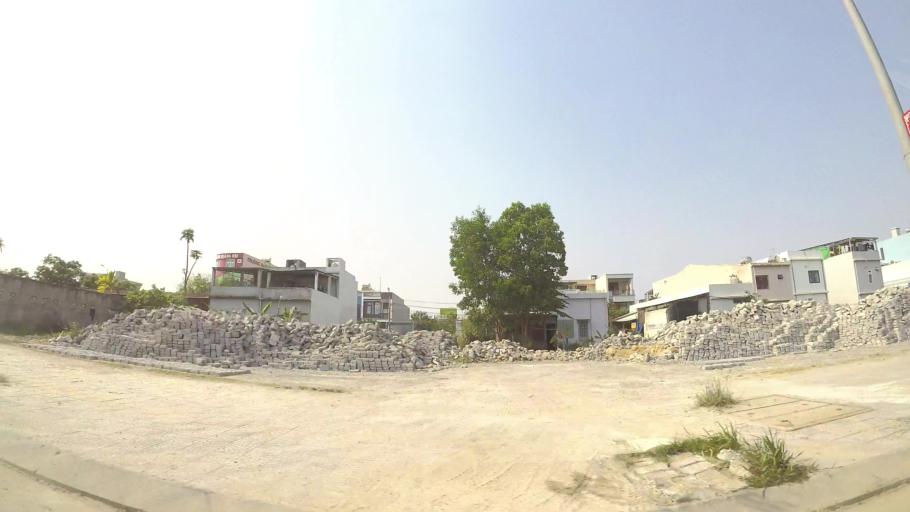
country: VN
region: Da Nang
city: Cam Le
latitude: 16.0091
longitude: 108.2025
